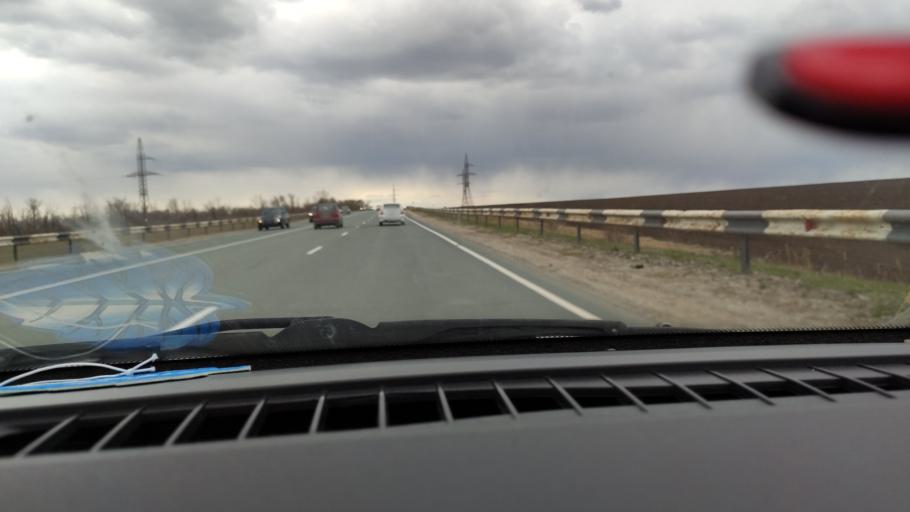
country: RU
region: Saratov
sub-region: Saratovskiy Rayon
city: Saratov
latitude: 51.7466
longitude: 46.0549
